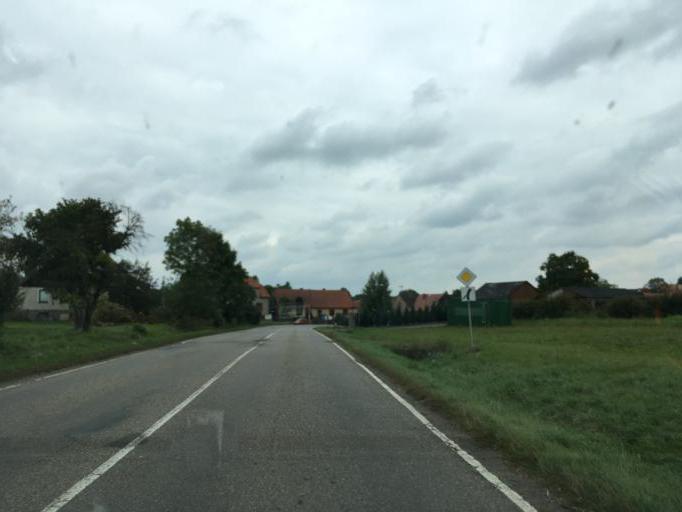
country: CZ
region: Central Bohemia
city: Cechtice
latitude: 49.6265
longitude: 15.0450
